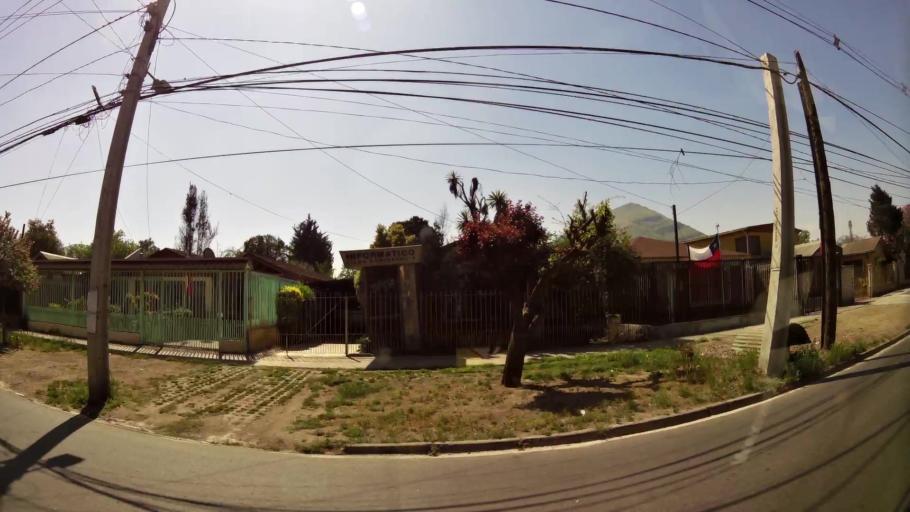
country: CL
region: Santiago Metropolitan
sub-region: Provincia de Santiago
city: Lo Prado
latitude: -33.4067
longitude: -70.7213
